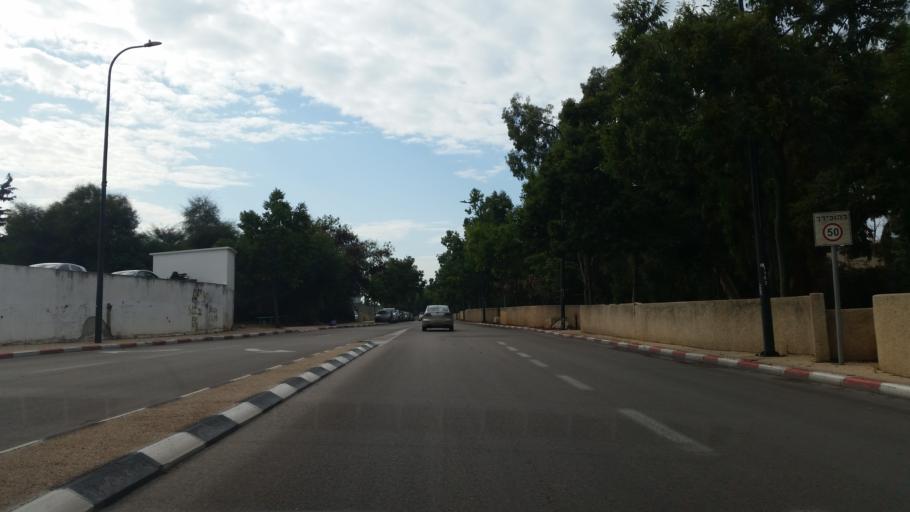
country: IL
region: Tel Aviv
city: Herzliya Pituah
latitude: 32.1664
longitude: 34.8087
